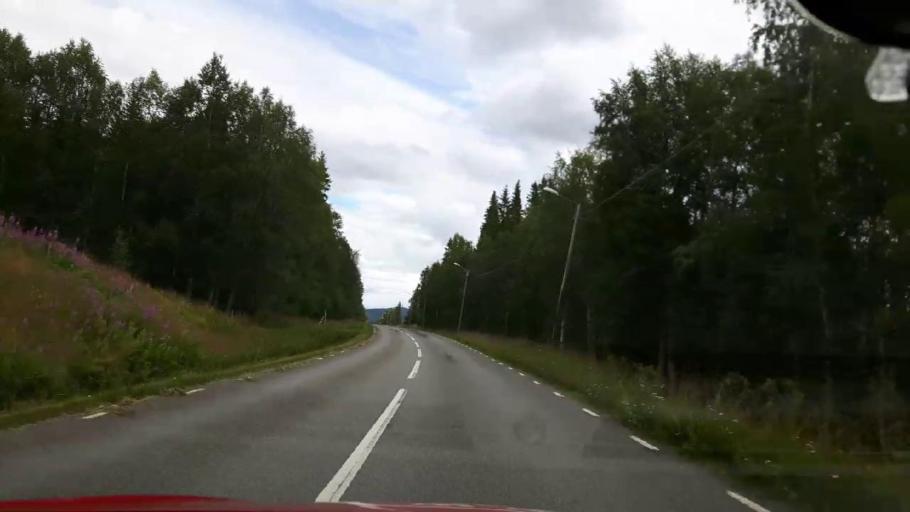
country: NO
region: Nord-Trondelag
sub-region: Lierne
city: Sandvika
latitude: 64.3903
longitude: 14.3806
